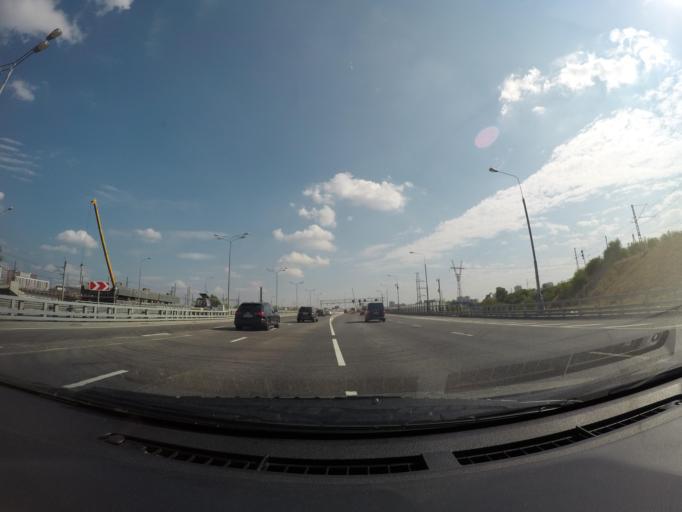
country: RU
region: Moscow
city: Zapadnoye Degunino
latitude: 55.8540
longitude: 37.5440
